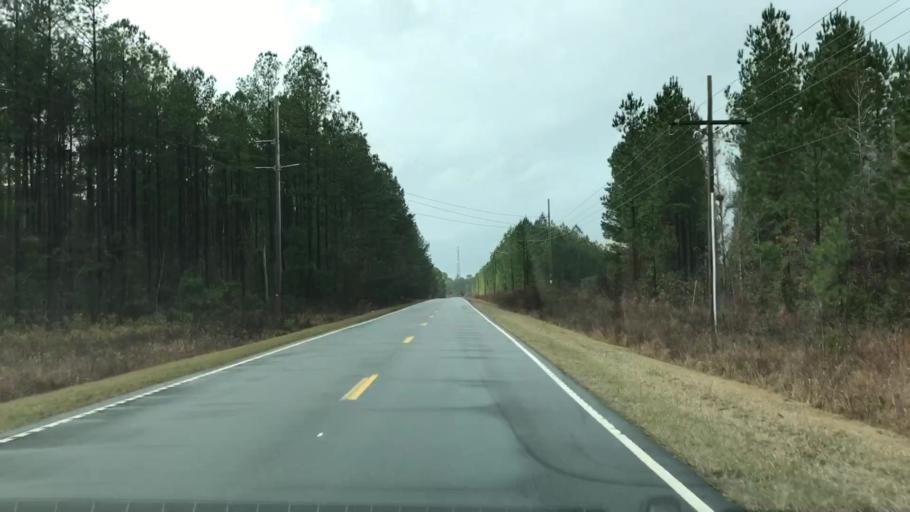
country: US
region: South Carolina
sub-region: Florence County
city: Johnsonville
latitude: 33.6762
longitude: -79.3422
